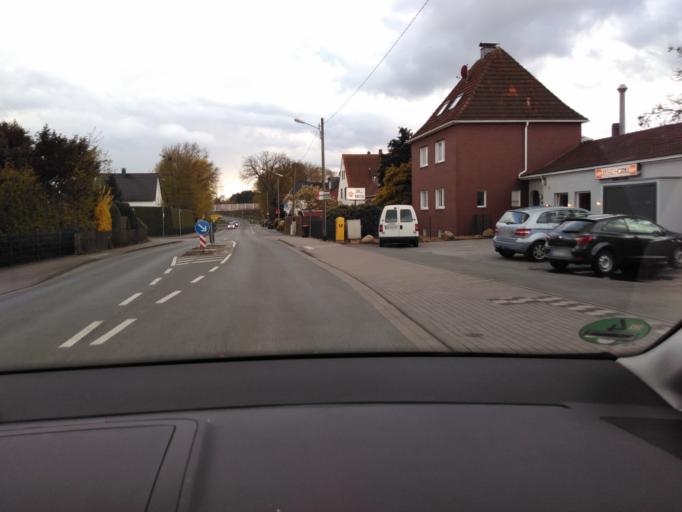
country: DE
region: North Rhine-Westphalia
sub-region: Regierungsbezirk Detmold
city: Bielefeld
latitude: 51.9635
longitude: 8.5036
